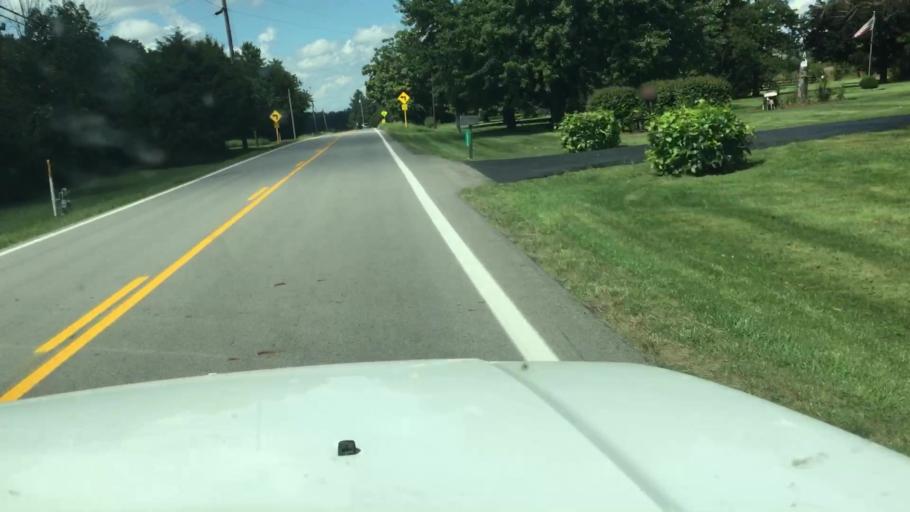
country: US
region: Ohio
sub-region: Madison County
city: Mount Sterling
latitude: 39.7124
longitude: -83.2449
